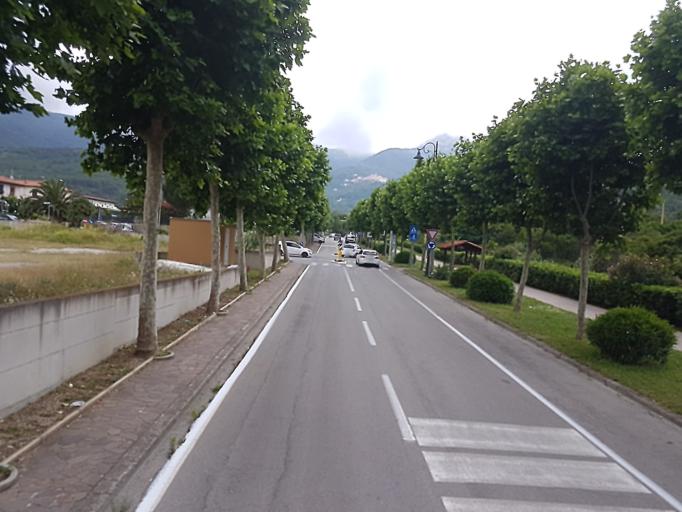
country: IT
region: Tuscany
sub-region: Provincia di Livorno
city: Marciana Marina
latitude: 42.8058
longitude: 10.1927
